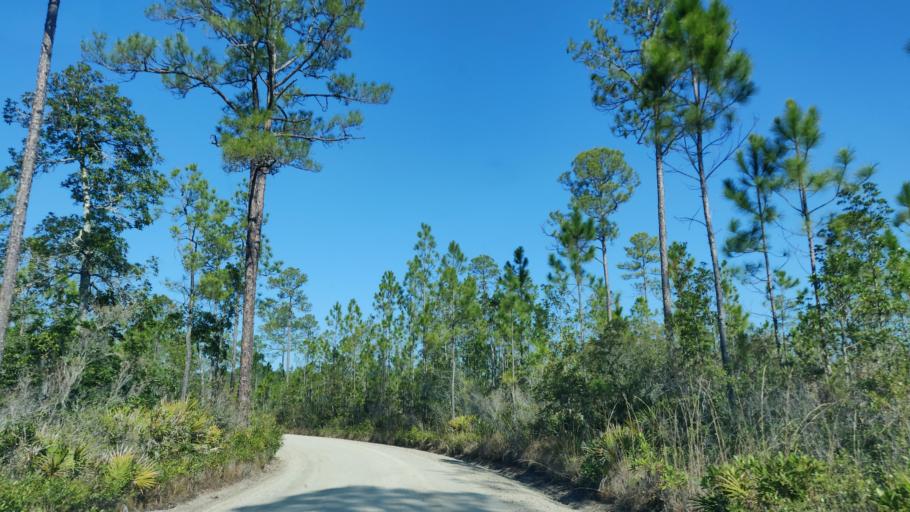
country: US
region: Florida
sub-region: Duval County
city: Baldwin
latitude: 30.1700
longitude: -81.9522
